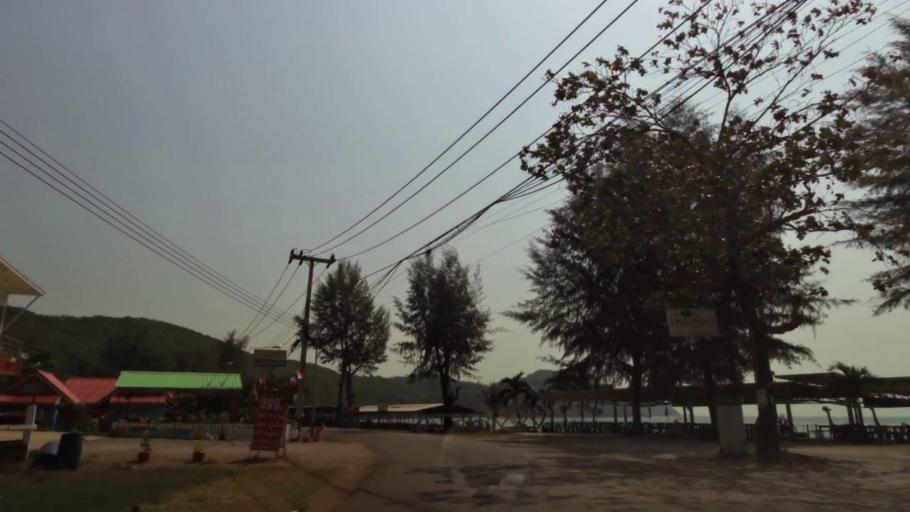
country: TH
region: Chanthaburi
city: Tha Mai
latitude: 12.5333
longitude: 101.9423
